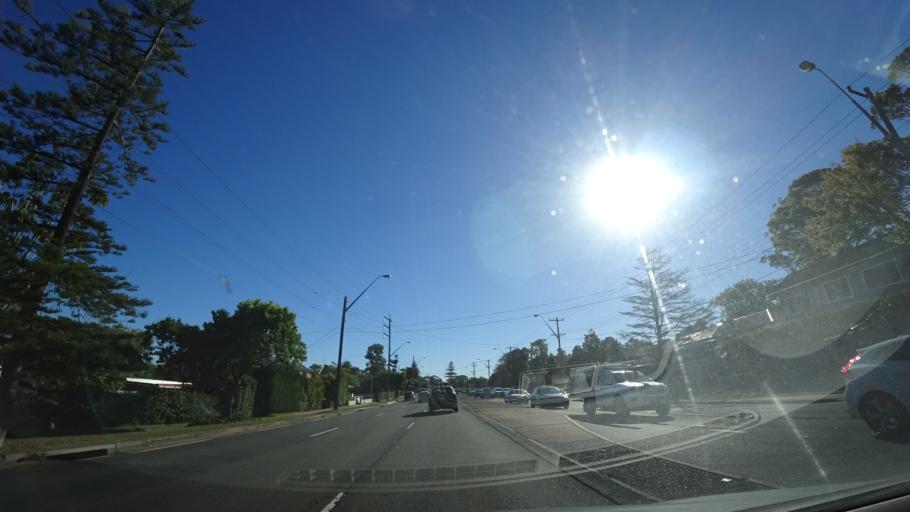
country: AU
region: New South Wales
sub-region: Warringah
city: Forestville
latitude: -33.7547
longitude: 151.2226
